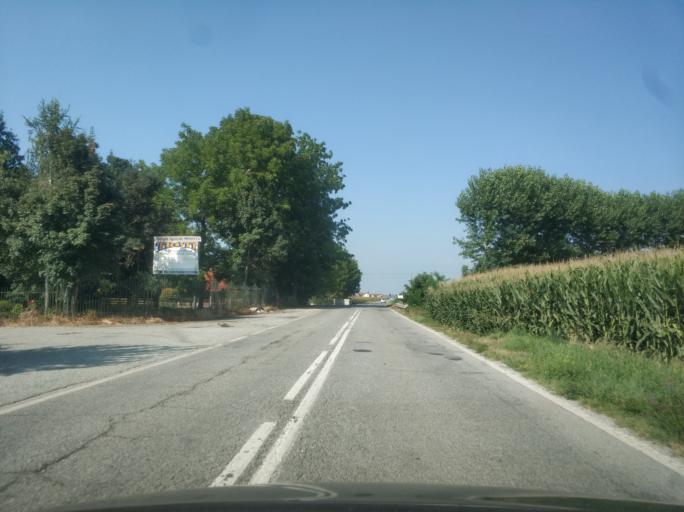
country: IT
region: Piedmont
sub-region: Provincia di Cuneo
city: Centallo
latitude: 44.5270
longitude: 7.6047
